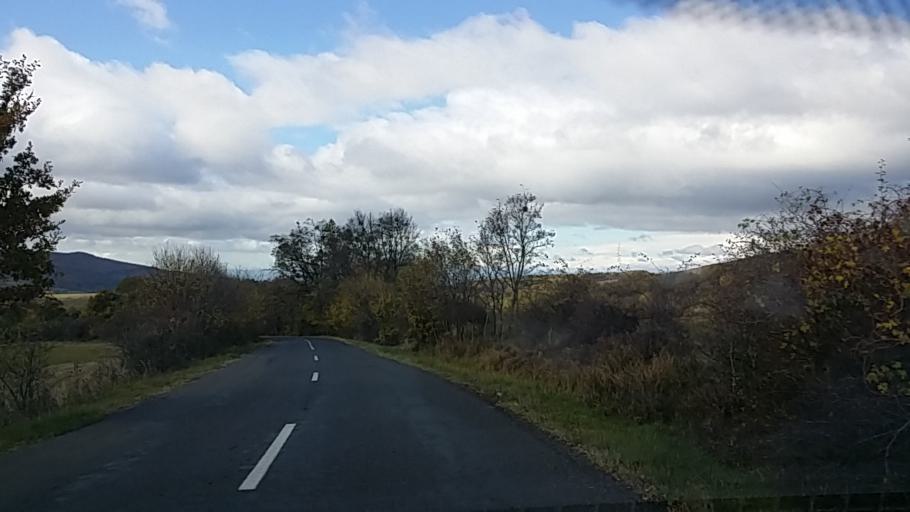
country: HU
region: Borsod-Abauj-Zemplen
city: Gonc
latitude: 48.4867
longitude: 21.3868
